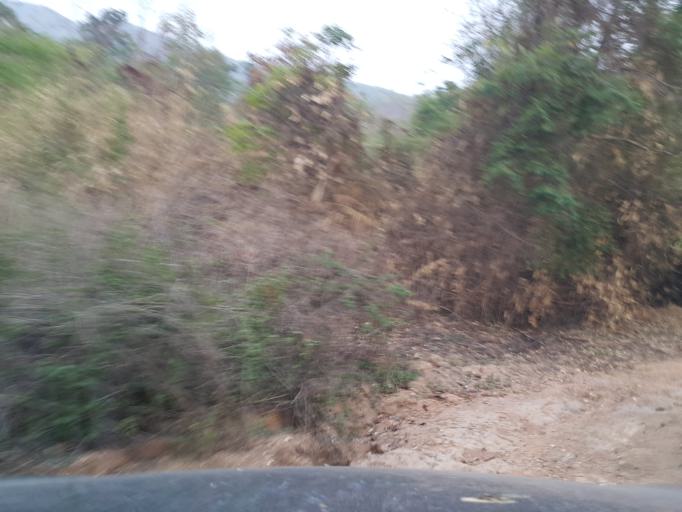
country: TH
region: Lamphun
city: Thung Hua Chang
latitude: 17.9106
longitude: 99.0794
